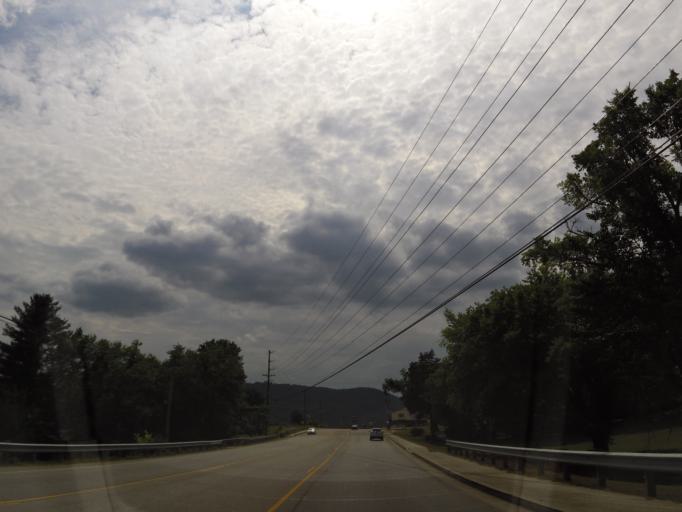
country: US
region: Tennessee
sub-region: Marion County
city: Kimball
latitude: 35.0445
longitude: -85.6795
